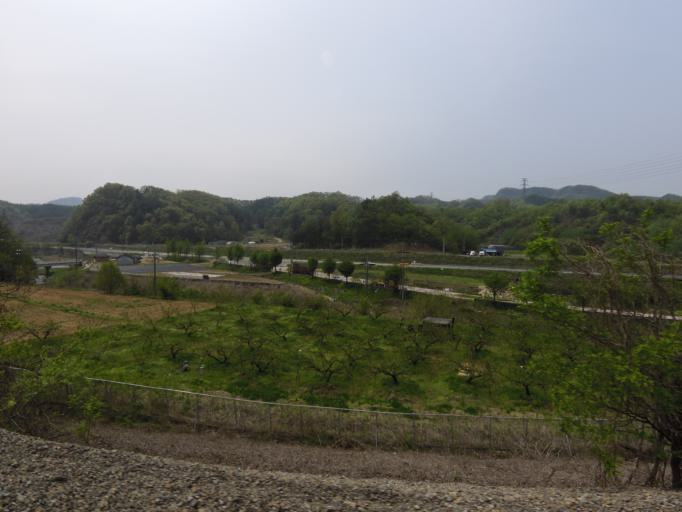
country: KR
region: Chungcheongbuk-do
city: Okcheon
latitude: 36.3235
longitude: 127.5453
